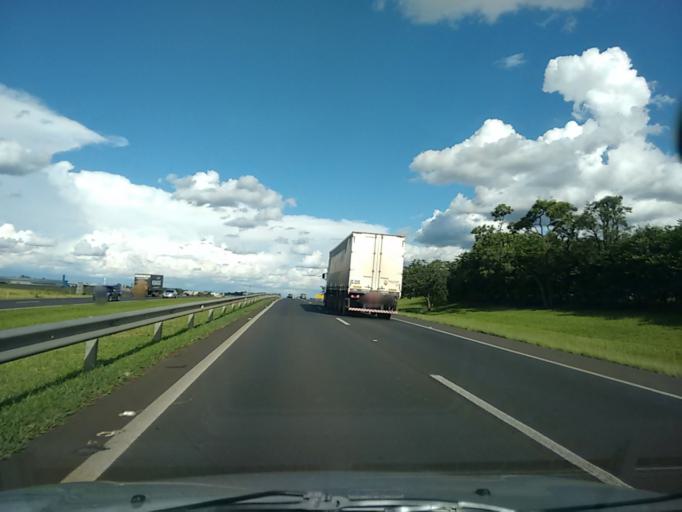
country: BR
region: Sao Paulo
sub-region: Sao Carlos
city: Sao Carlos
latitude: -21.9807
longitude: -47.9191
